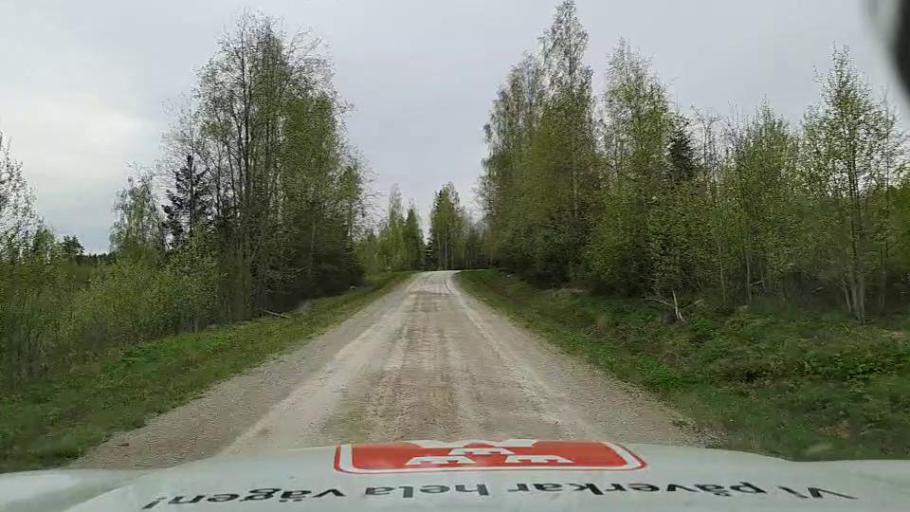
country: SE
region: Jaemtland
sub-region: Bergs Kommun
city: Hoverberg
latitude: 62.6787
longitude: 14.7669
